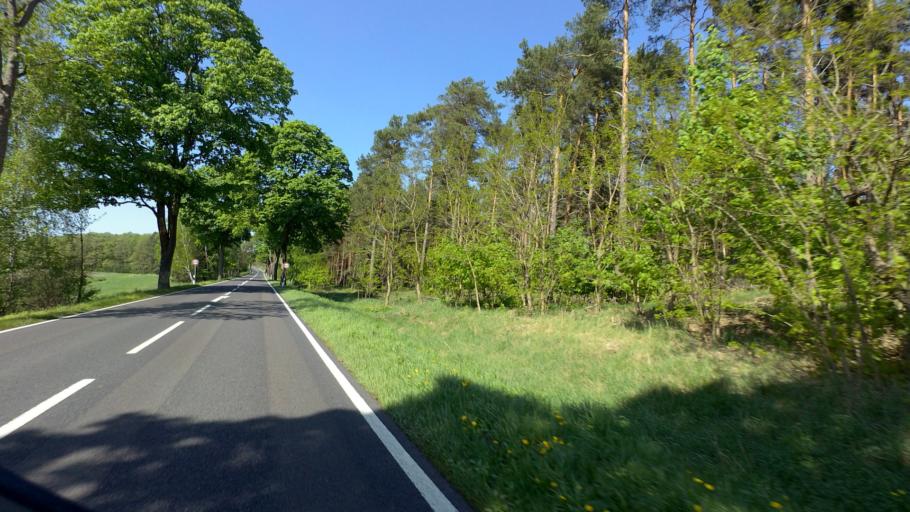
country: DE
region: Brandenburg
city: Friedland
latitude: 52.0621
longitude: 14.2779
